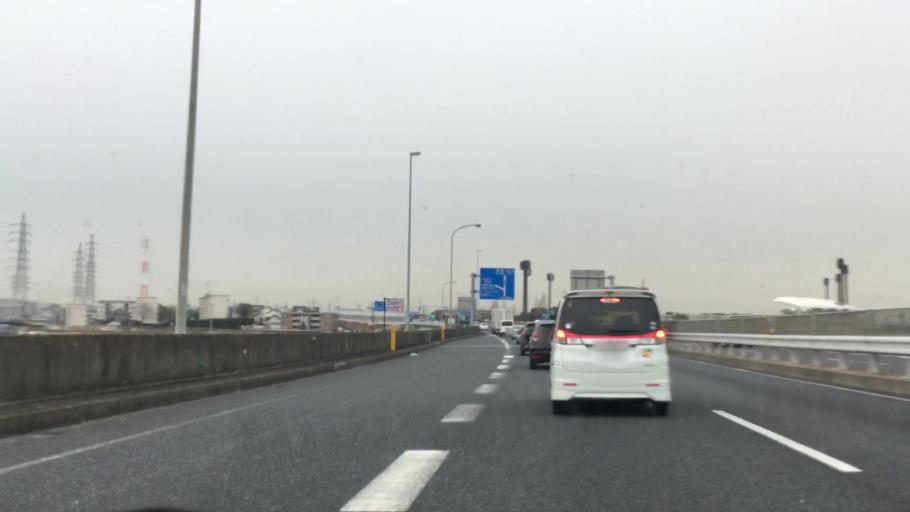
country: JP
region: Aichi
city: Chiryu
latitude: 35.0230
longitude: 137.0121
